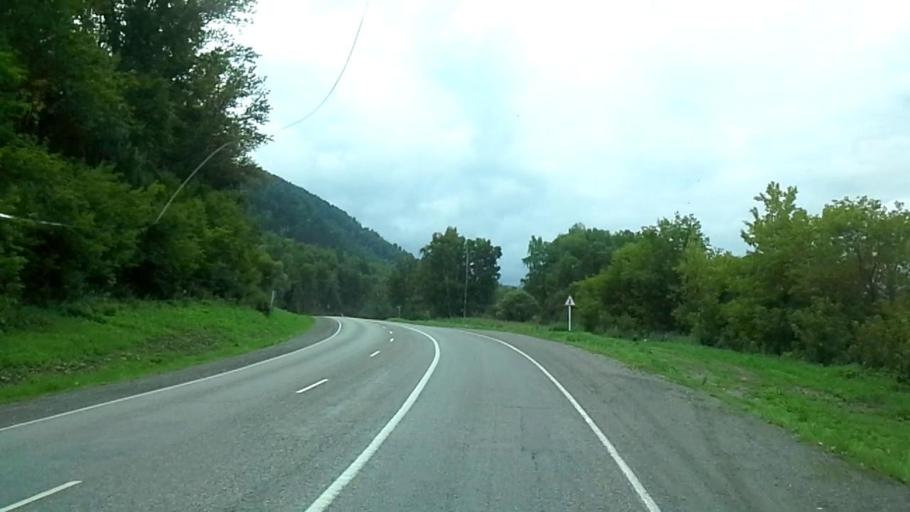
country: RU
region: Altay
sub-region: Mayminskiy Rayon
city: Manzherok
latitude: 51.8624
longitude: 85.7611
